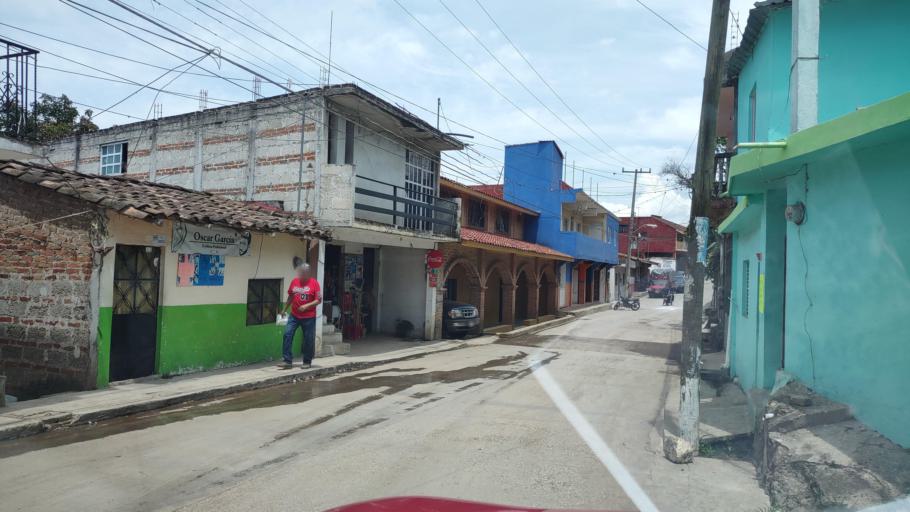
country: MX
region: Veracruz
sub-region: Emiliano Zapata
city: Jacarandas
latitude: 19.4659
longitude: -96.8356
